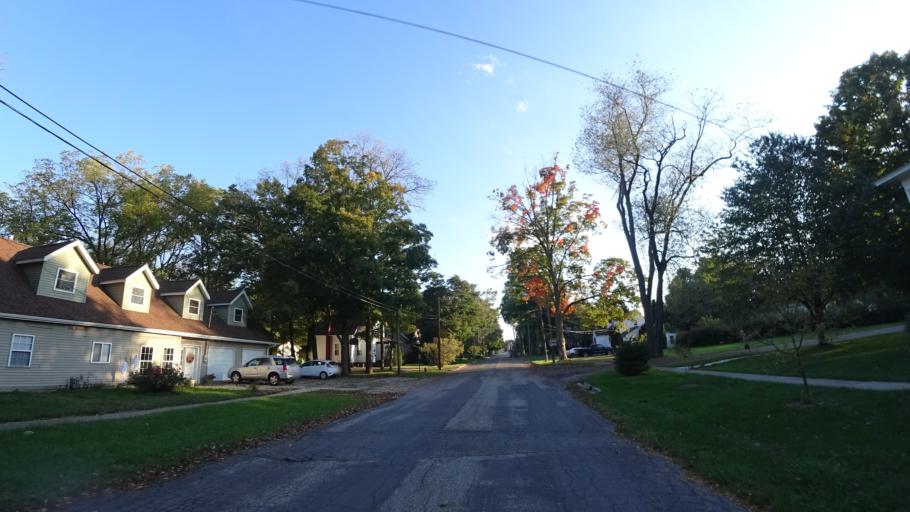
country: US
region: Michigan
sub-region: Saint Joseph County
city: Three Rivers
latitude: 41.9466
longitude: -85.6419
